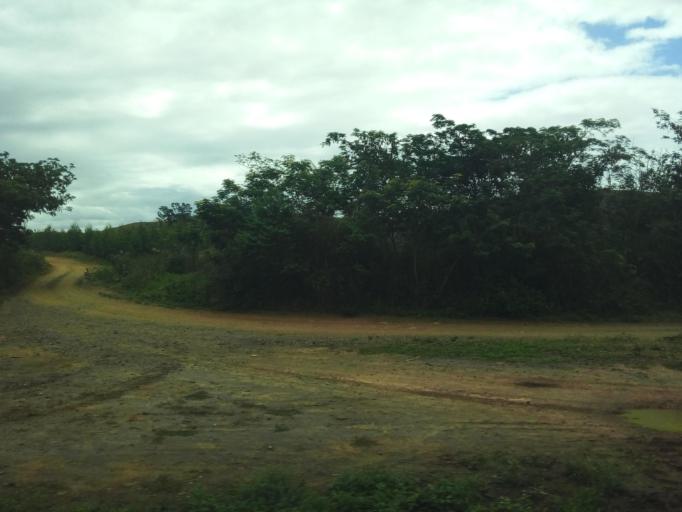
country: BR
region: Minas Gerais
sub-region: Governador Valadares
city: Governador Valadares
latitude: -19.0877
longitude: -42.1629
